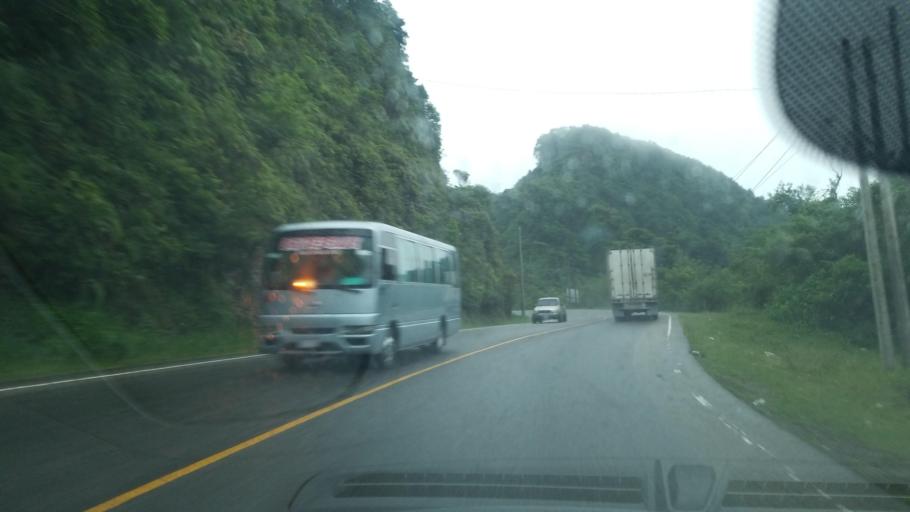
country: HN
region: Ocotepeque
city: La Labor
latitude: 14.4654
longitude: -89.0707
